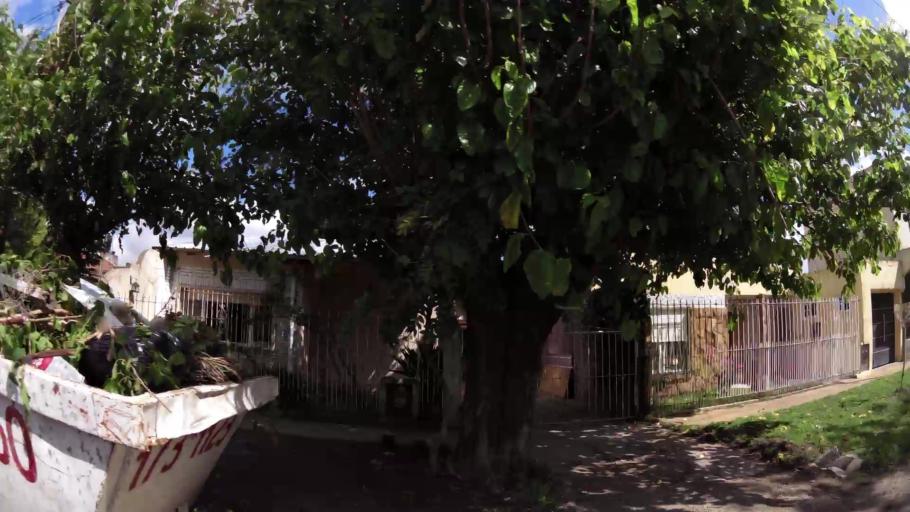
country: AR
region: Buenos Aires
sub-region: Partido de Quilmes
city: Quilmes
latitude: -34.8312
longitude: -58.1759
